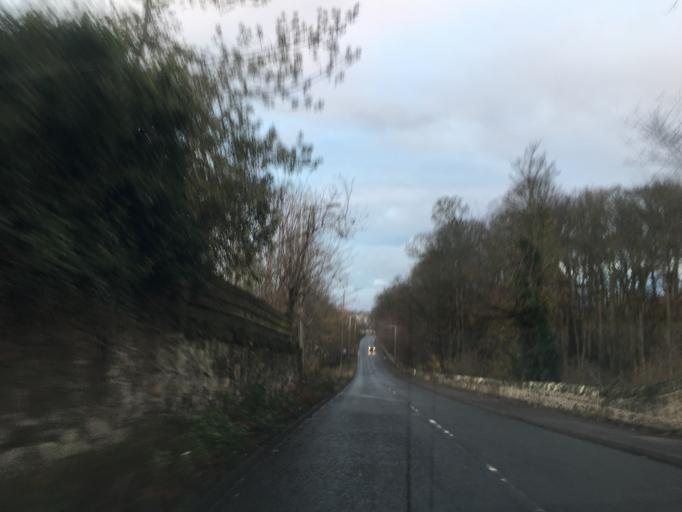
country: GB
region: Scotland
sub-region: Edinburgh
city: Colinton
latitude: 55.9522
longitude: -3.2565
